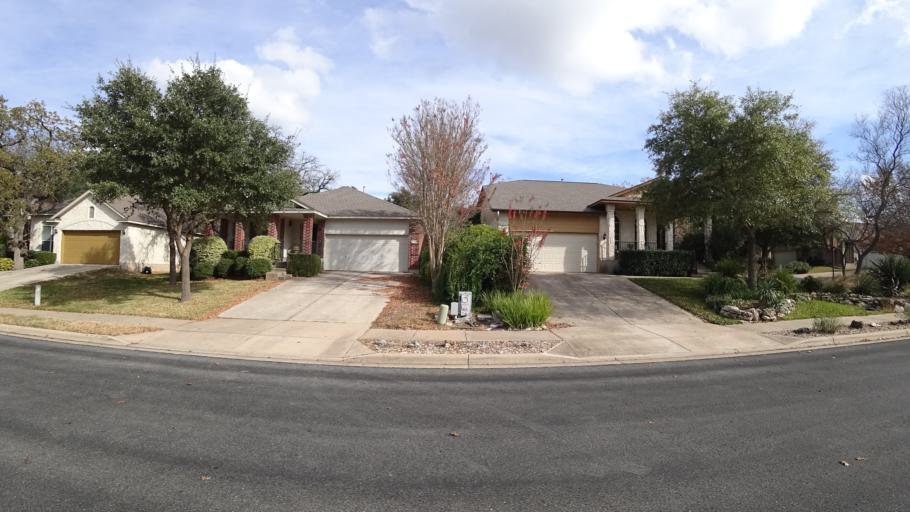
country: US
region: Texas
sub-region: Williamson County
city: Brushy Creek
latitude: 30.5077
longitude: -97.7487
